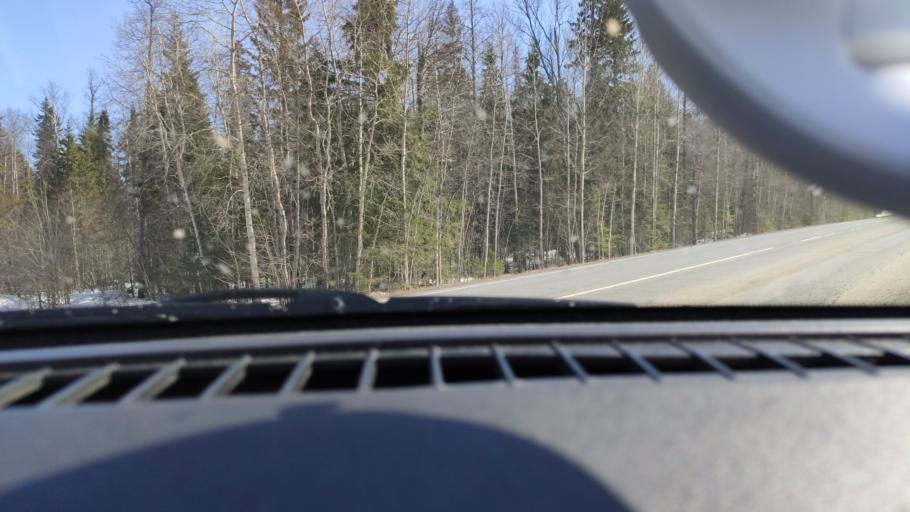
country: RU
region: Perm
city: Perm
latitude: 58.2205
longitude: 56.1675
